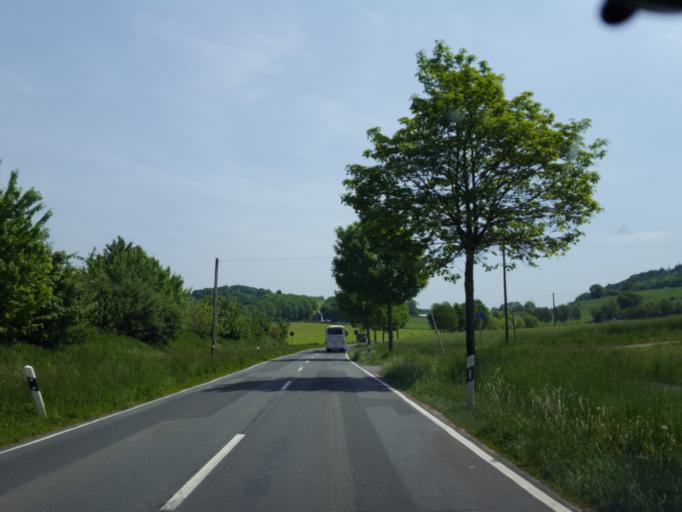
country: DE
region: North Rhine-Westphalia
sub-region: Regierungsbezirk Arnsberg
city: Brilon
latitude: 51.4049
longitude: 8.6075
